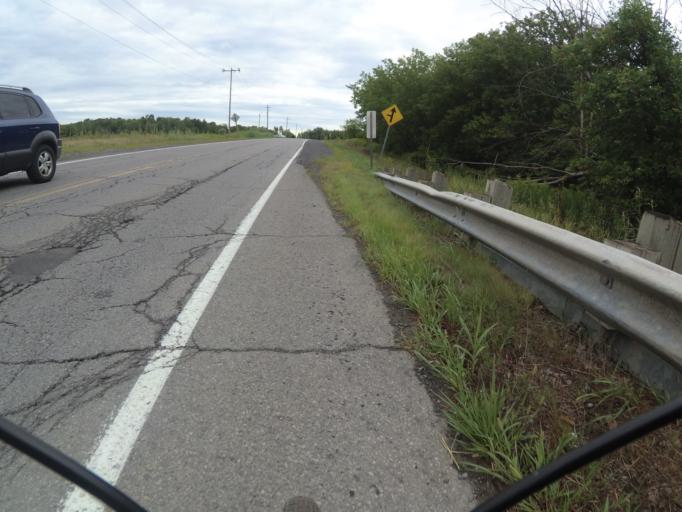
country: CA
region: Ontario
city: Bourget
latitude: 45.3947
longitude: -75.2808
